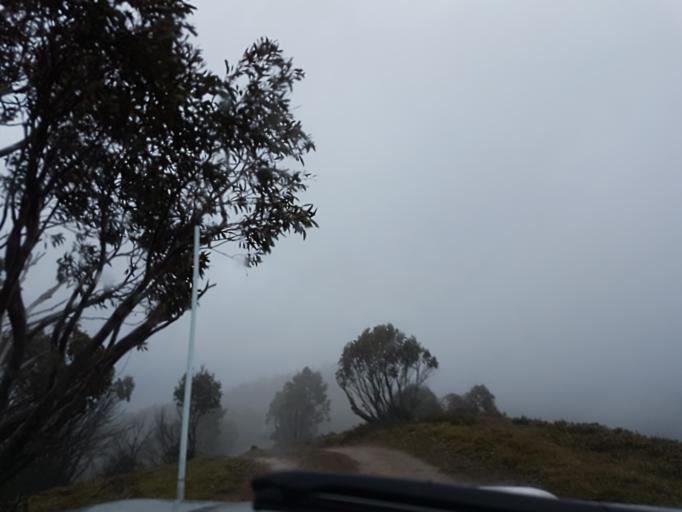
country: AU
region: Victoria
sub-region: Alpine
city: Mount Beauty
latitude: -37.0905
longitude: 147.0701
